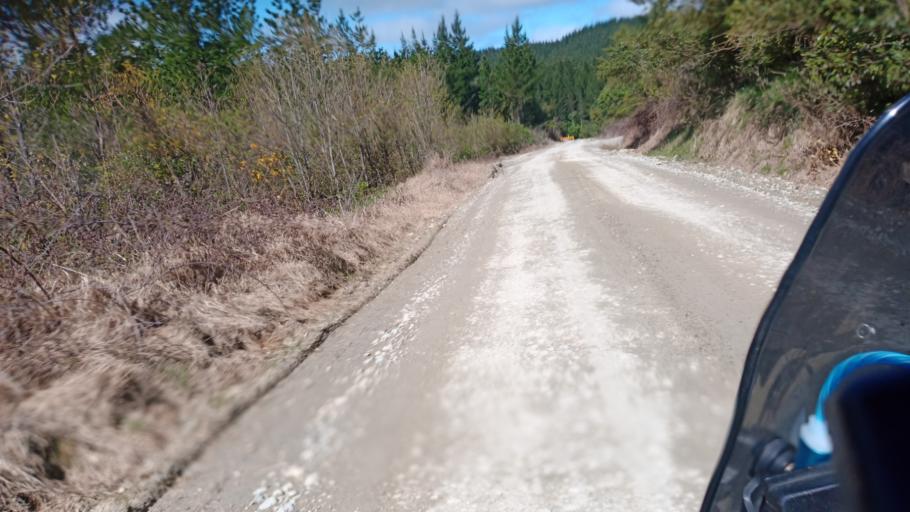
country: NZ
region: Gisborne
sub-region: Gisborne District
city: Gisborne
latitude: -38.9098
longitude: 177.8150
